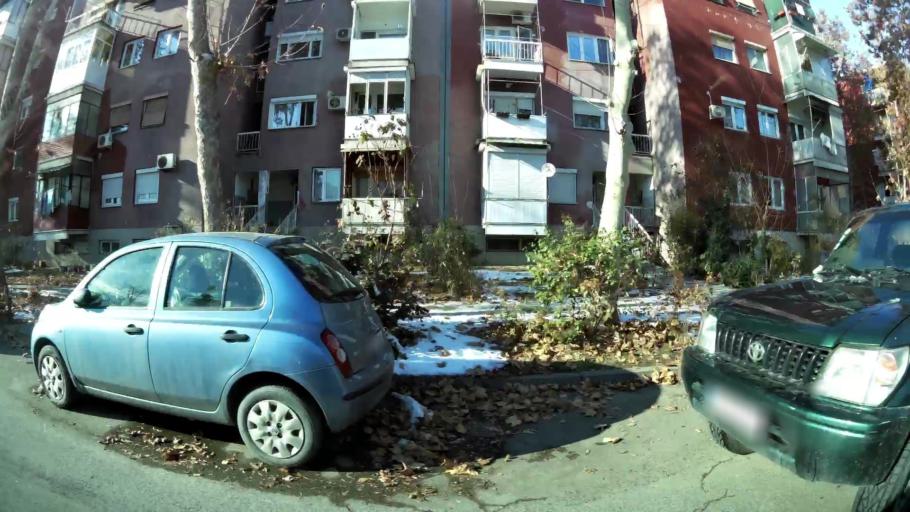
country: MK
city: Krushopek
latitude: 42.0034
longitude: 21.3724
